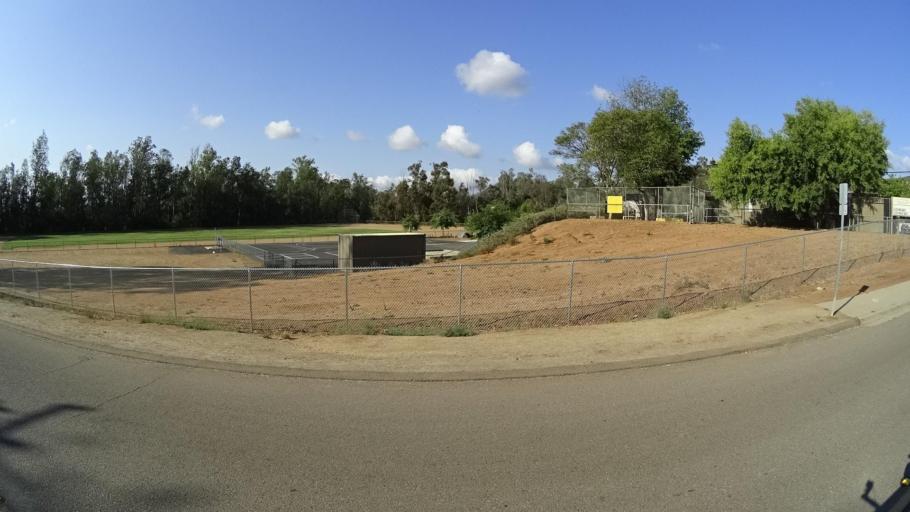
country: US
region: California
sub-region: San Diego County
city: Eucalyptus Hills
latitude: 32.8916
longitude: -116.9459
